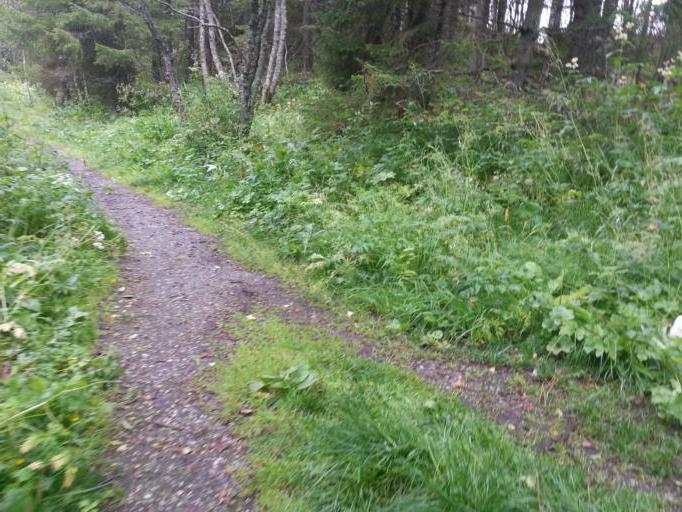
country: NO
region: Troms
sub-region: Tromso
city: Tromso
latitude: 69.6334
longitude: 18.9122
